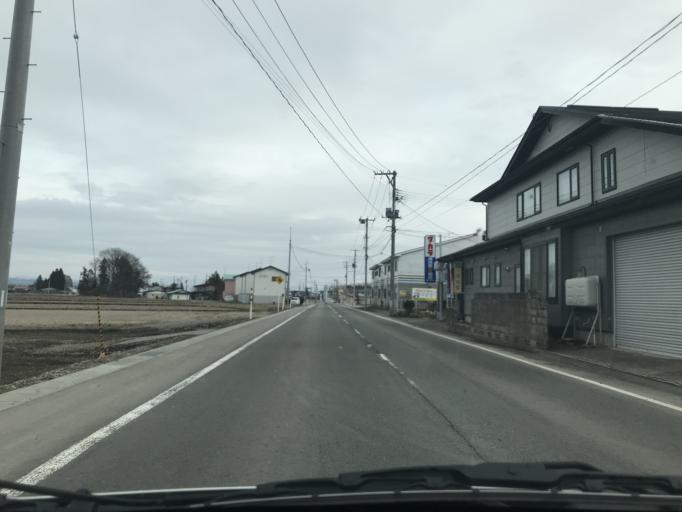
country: JP
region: Iwate
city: Kitakami
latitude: 39.3069
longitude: 141.0282
